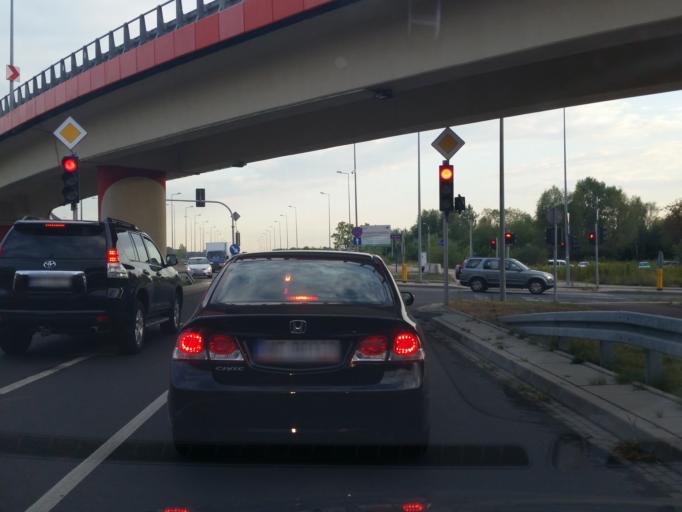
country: PL
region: Masovian Voivodeship
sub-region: Warszawa
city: Wlochy
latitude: 52.1677
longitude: 20.9853
